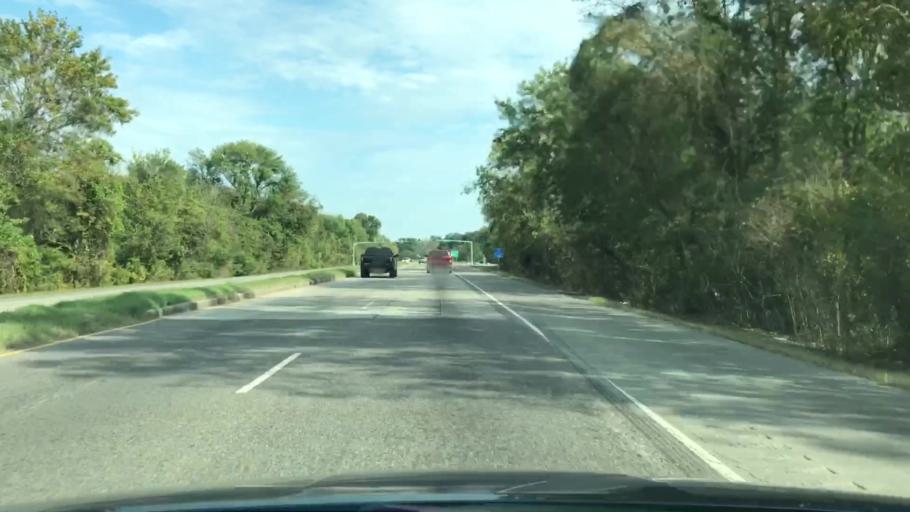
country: US
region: Louisiana
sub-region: Jefferson Parish
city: Avondale
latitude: 29.9093
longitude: -90.1939
